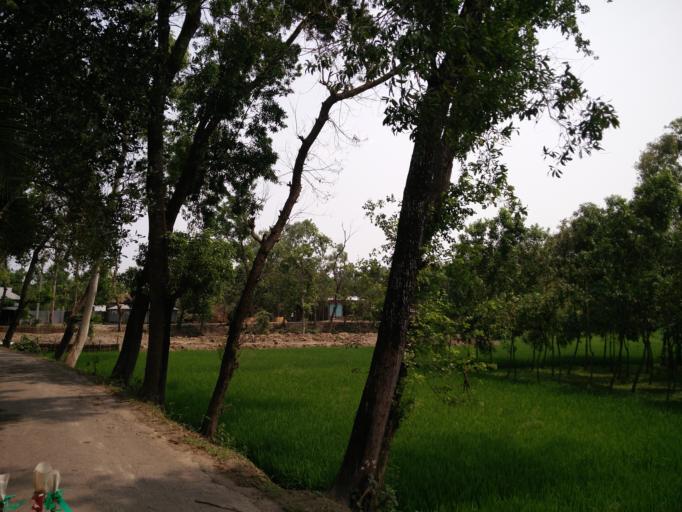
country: BD
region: Dhaka
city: Sherpur
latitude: 24.9334
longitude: 90.1674
